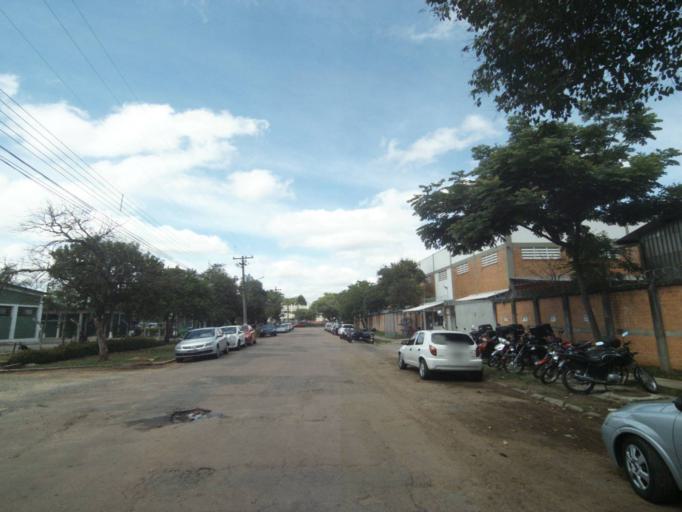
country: BR
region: Parana
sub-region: Curitiba
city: Curitiba
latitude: -25.4928
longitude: -49.3328
